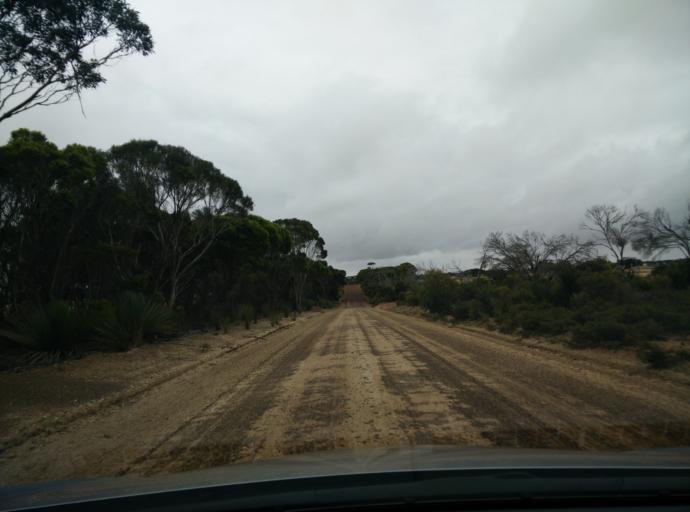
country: AU
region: South Australia
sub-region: Kangaroo Island
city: Kingscote
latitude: -35.8571
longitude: 137.4633
